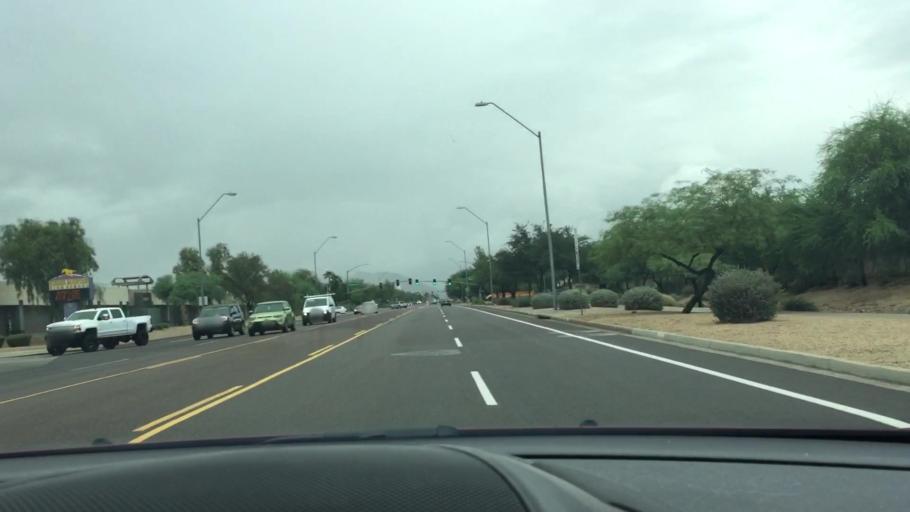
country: US
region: Arizona
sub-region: Maricopa County
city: Sun City
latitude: 33.6764
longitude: -112.2378
